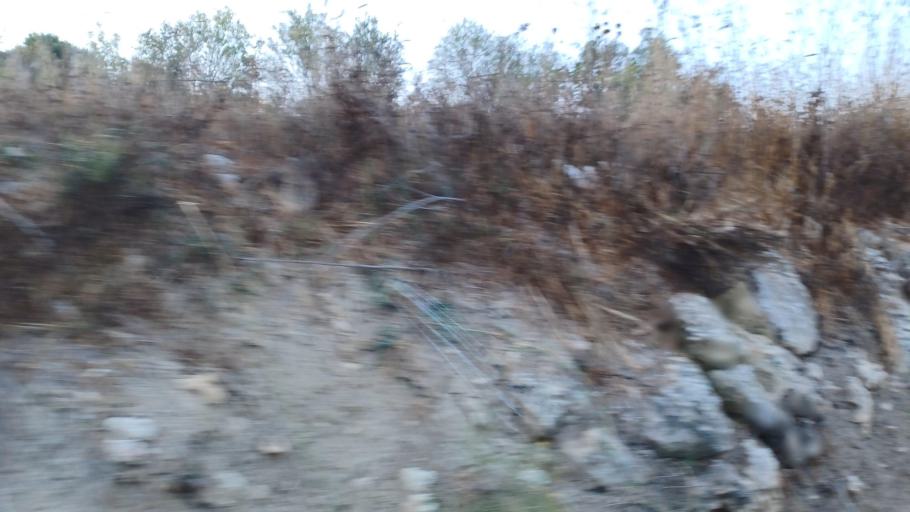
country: CY
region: Pafos
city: Tala
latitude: 34.8862
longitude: 32.5005
